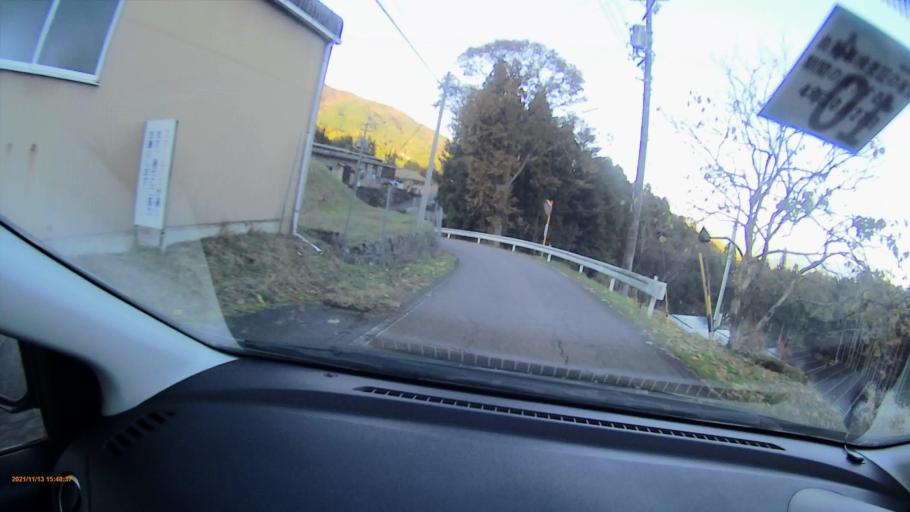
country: JP
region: Gifu
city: Nakatsugawa
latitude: 35.5959
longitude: 137.4050
